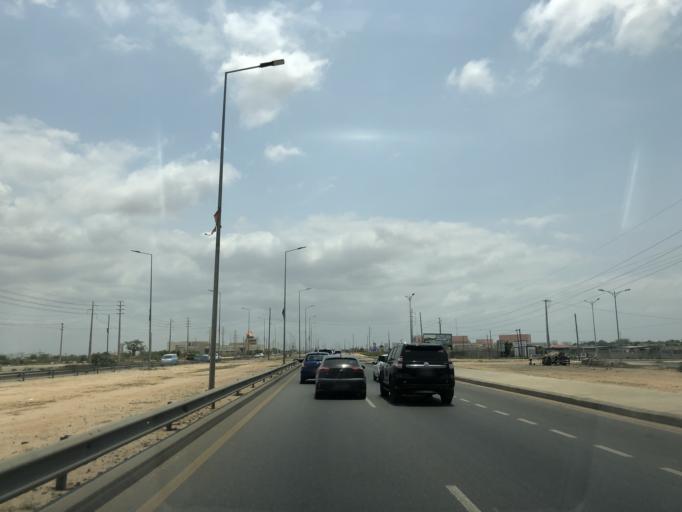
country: AO
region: Luanda
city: Luanda
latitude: -8.9536
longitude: 13.2584
